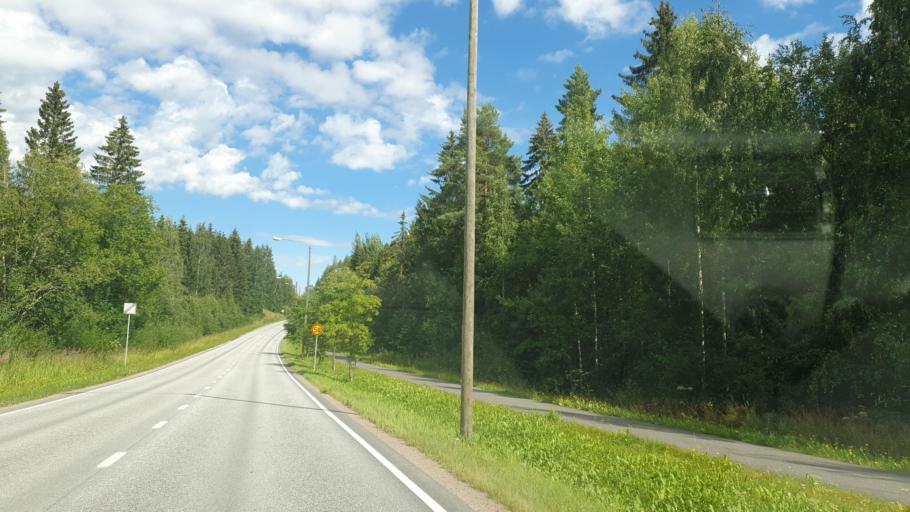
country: FI
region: Central Finland
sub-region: Jyvaeskylae
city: Muurame
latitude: 62.1385
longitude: 25.6898
